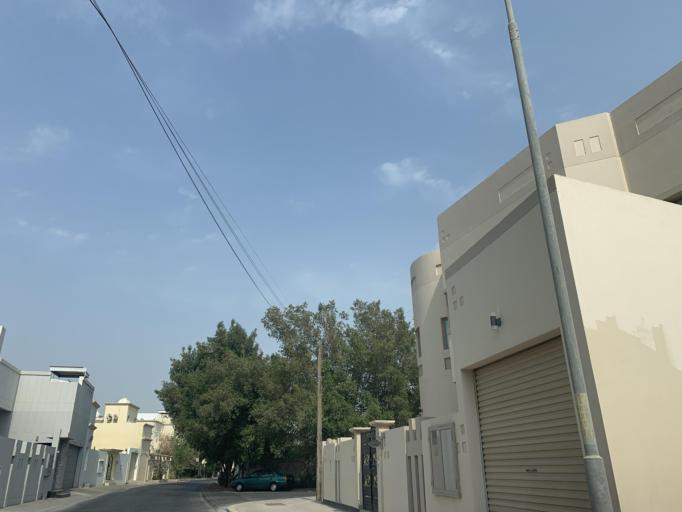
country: BH
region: Manama
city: Jidd Hafs
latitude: 26.2154
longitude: 50.4897
